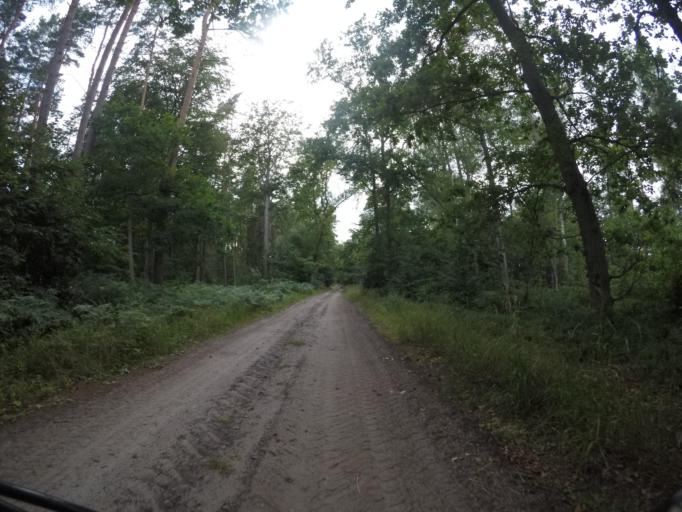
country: DE
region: Mecklenburg-Vorpommern
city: Lubtheen
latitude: 53.2491
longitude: 11.0309
